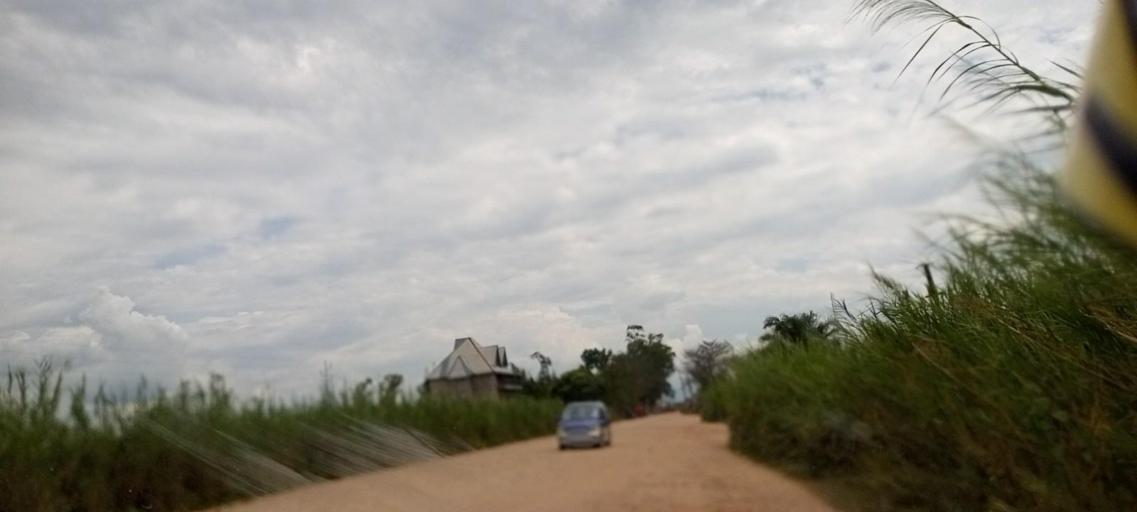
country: CD
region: South Kivu
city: Uvira
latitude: -3.3405
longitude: 29.2006
